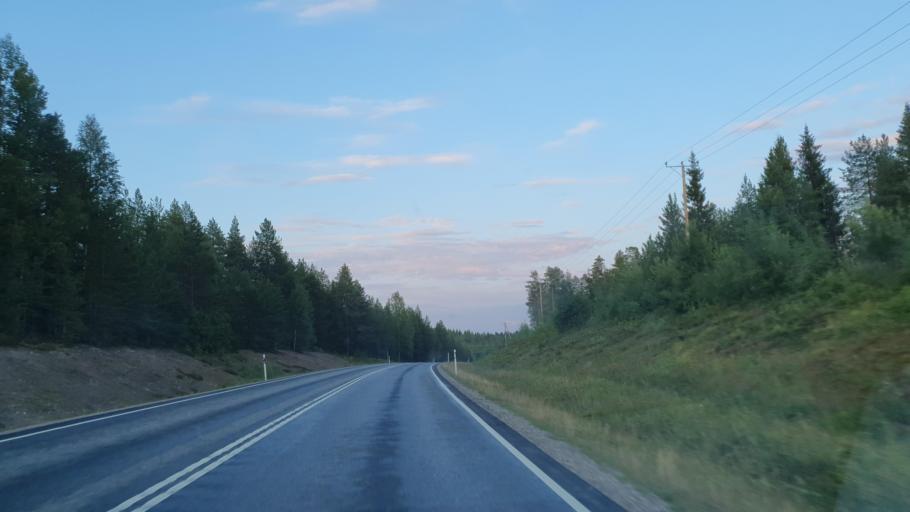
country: FI
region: Kainuu
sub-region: Kehys-Kainuu
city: Suomussalmi
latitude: 64.7840
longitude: 28.7746
